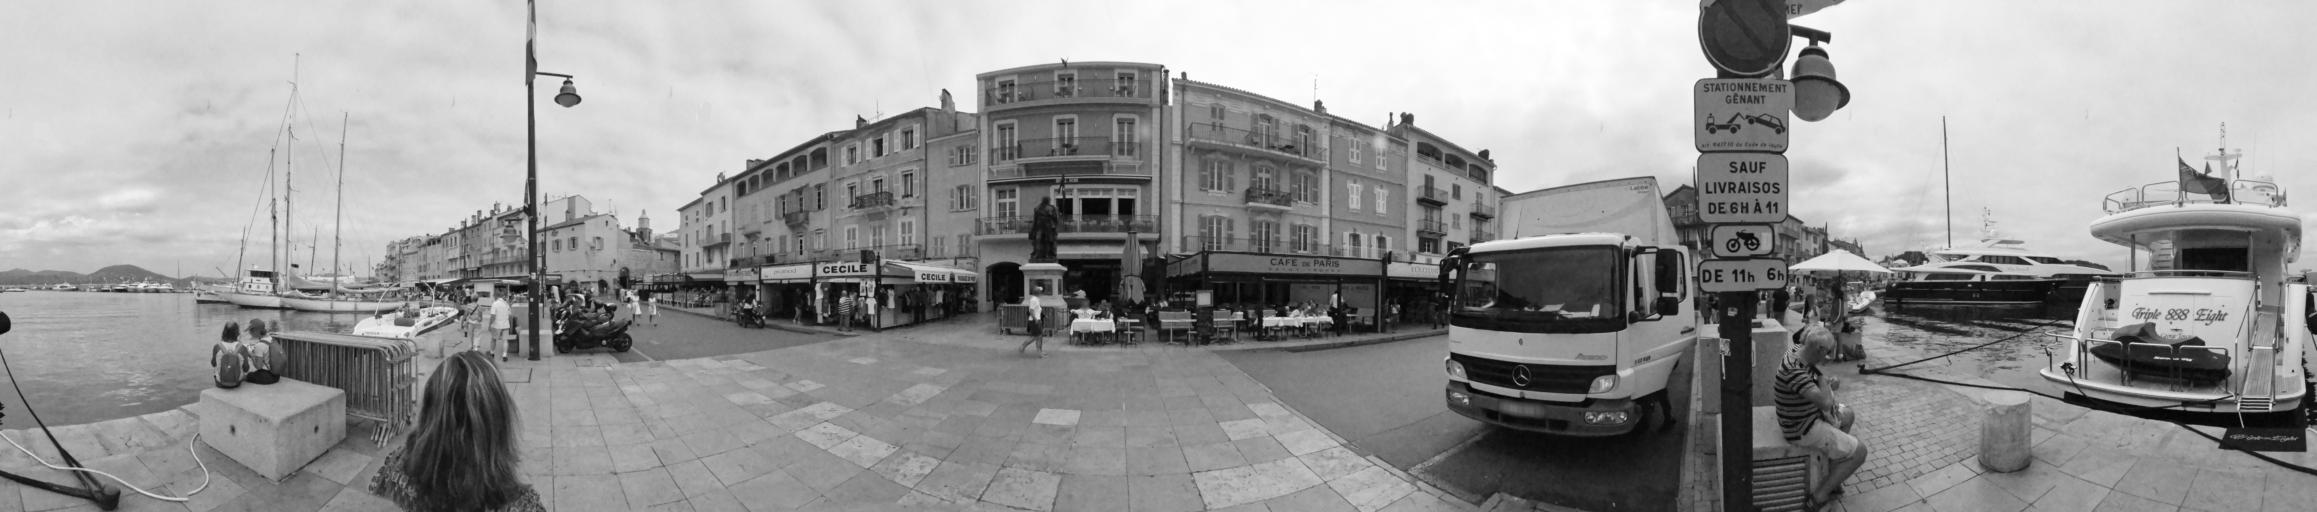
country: FR
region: Provence-Alpes-Cote d'Azur
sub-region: Departement du Var
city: Saint-Tropez
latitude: 43.2717
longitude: 6.6389
